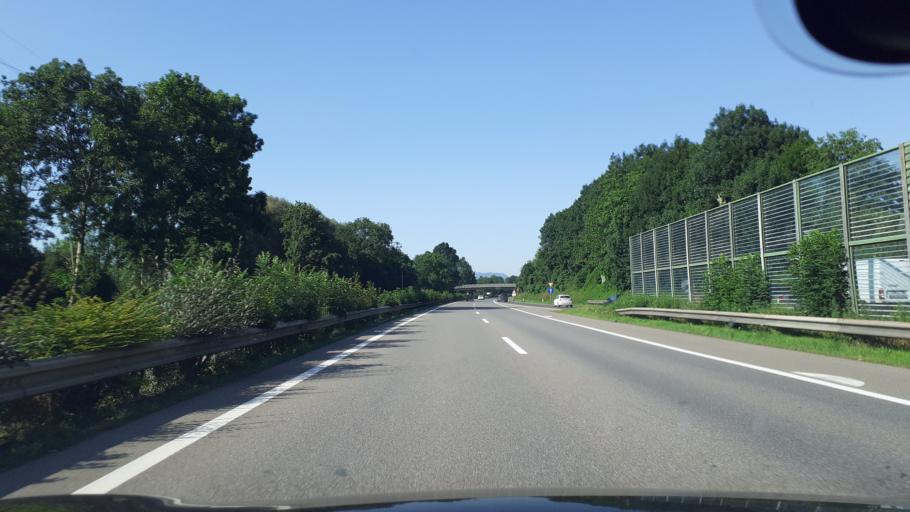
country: AT
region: Vorarlberg
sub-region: Politischer Bezirk Feldkirch
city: Altach
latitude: 47.3543
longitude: 9.6399
